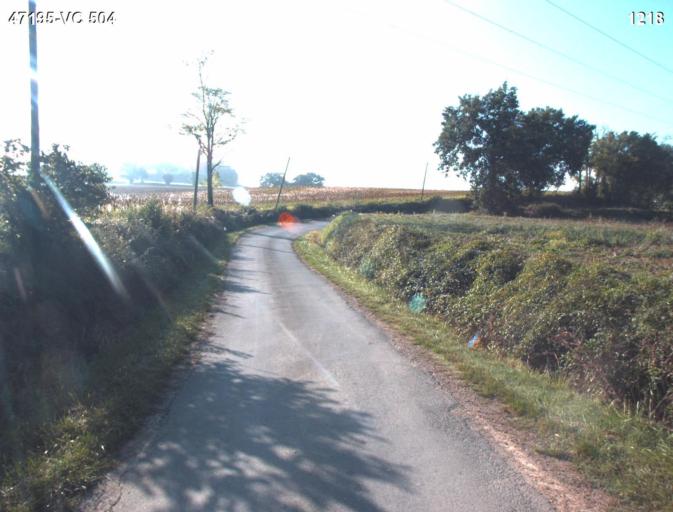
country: FR
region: Aquitaine
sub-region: Departement du Lot-et-Garonne
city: Nerac
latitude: 44.1576
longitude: 0.3342
